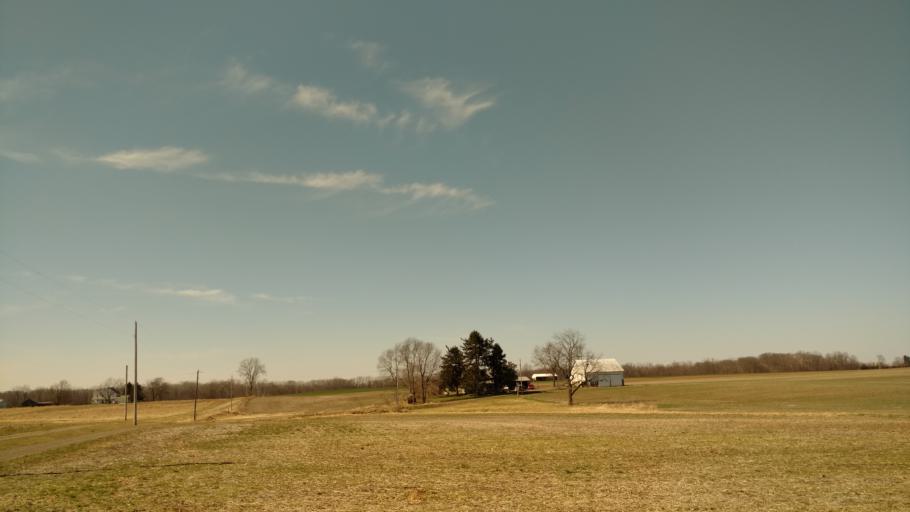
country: US
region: Ohio
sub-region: Marion County
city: Prospect
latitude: 40.5208
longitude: -83.1899
